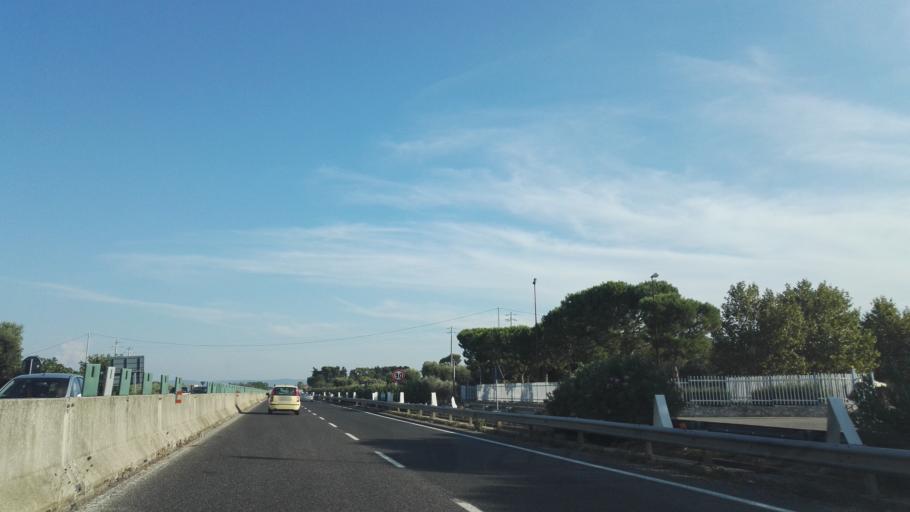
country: IT
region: Apulia
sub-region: Provincia di Bari
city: Monopoli
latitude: 40.9063
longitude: 17.3246
